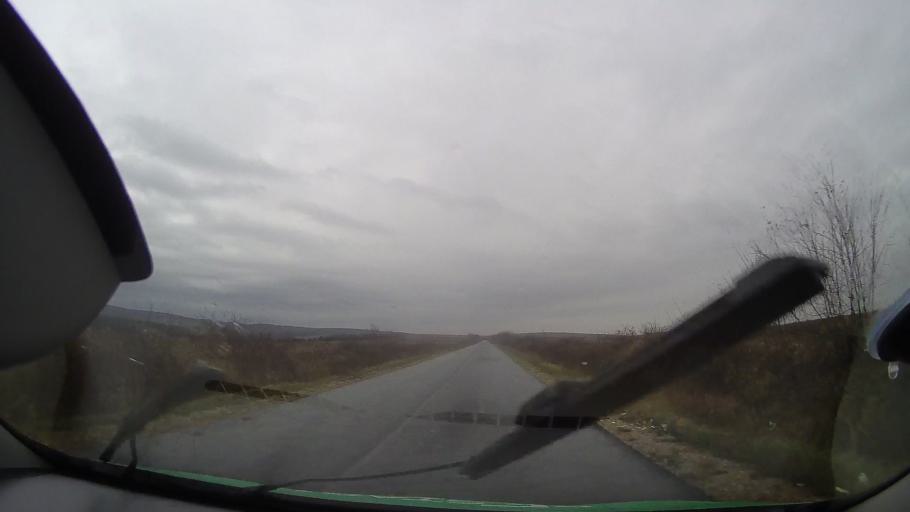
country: RO
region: Bihor
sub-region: Comuna Cociuba Mare
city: Cociuba Mare
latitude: 46.7008
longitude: 22.0356
